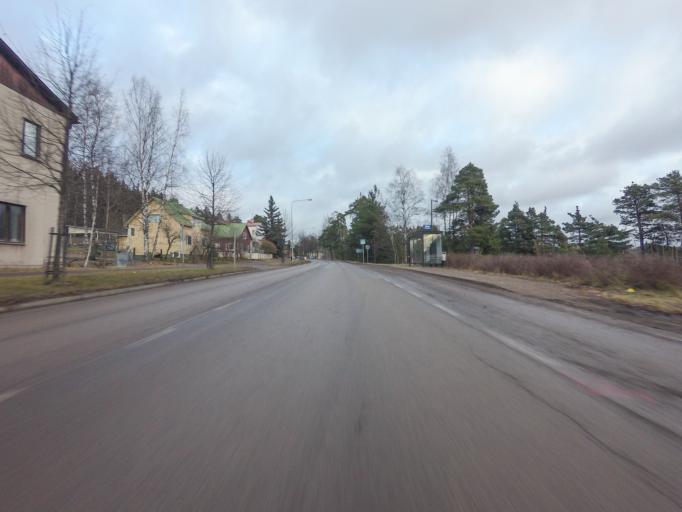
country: FI
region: Uusimaa
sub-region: Helsinki
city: Lohja
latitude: 60.2629
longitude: 24.1102
